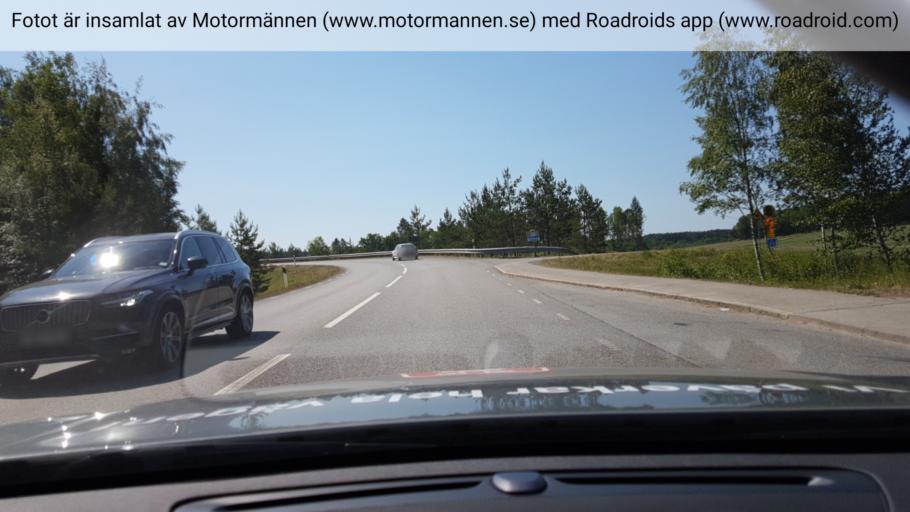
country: SE
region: Stockholm
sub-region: Norrtalje Kommun
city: Rimbo
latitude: 59.6966
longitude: 18.3699
